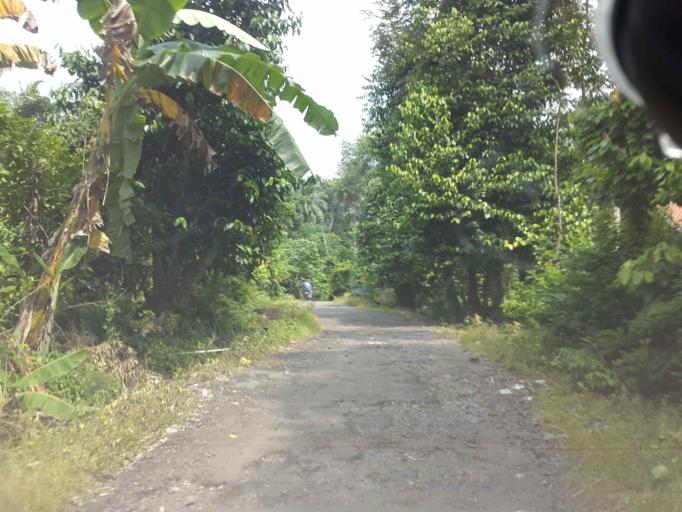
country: ID
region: Lampung
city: Penengahan
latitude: -5.8318
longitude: 105.6696
